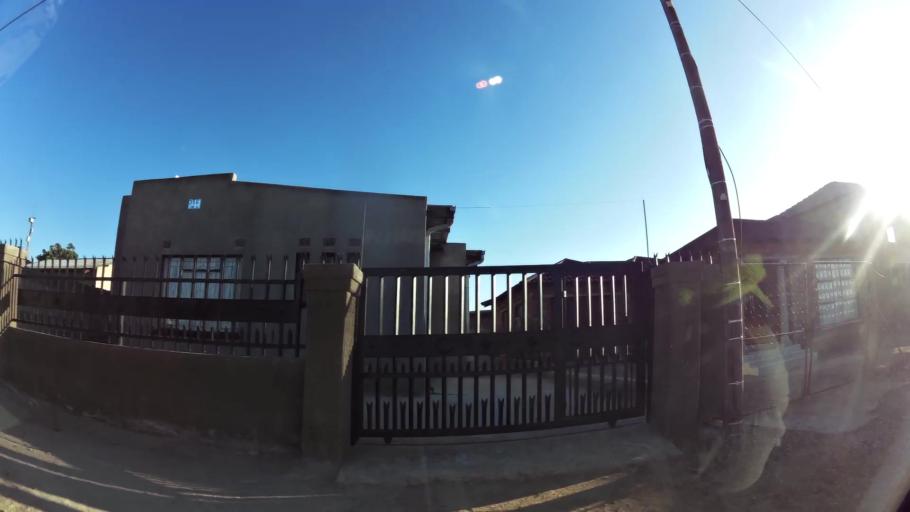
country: ZA
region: Limpopo
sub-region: Capricorn District Municipality
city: Polokwane
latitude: -23.8480
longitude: 29.3562
